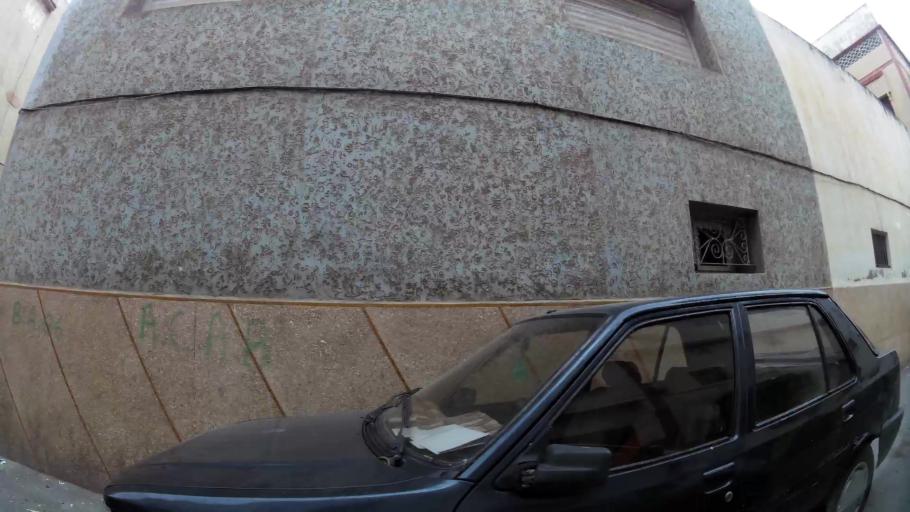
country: MA
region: Rabat-Sale-Zemmour-Zaer
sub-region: Rabat
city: Rabat
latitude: 33.9999
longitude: -6.8702
